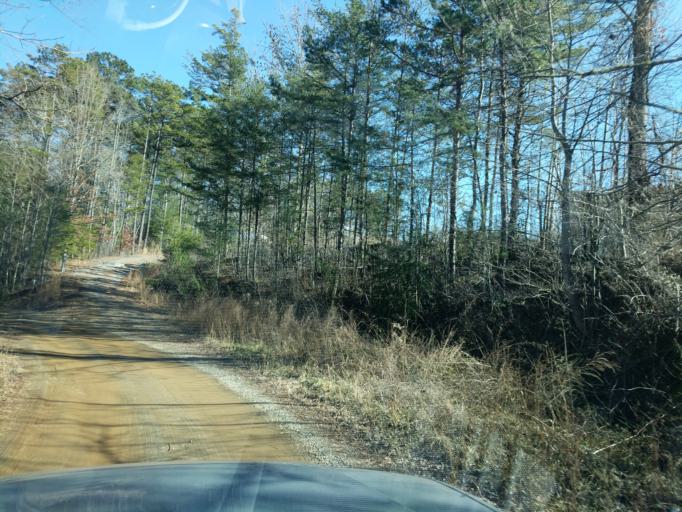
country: US
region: North Carolina
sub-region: Cherokee County
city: Murphy
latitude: 35.0288
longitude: -84.1589
